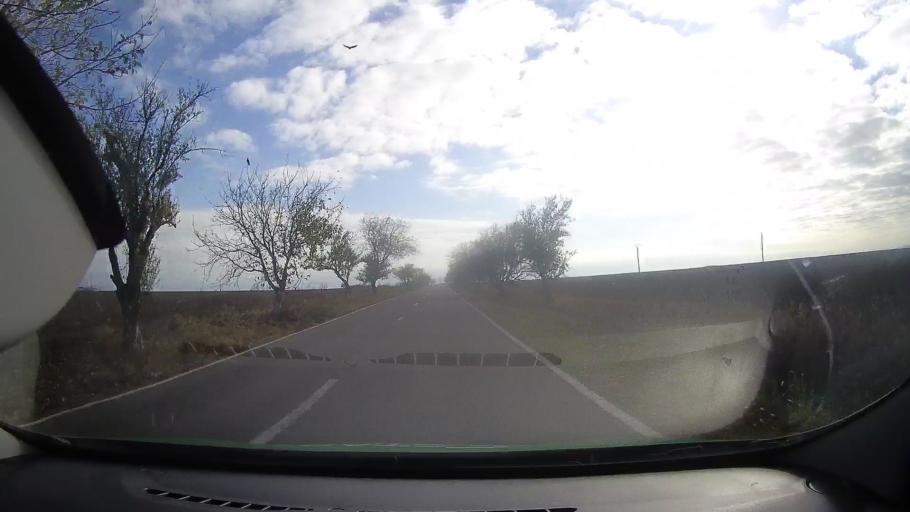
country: RO
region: Tulcea
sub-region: Comuna Bestepe
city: Bestepe
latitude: 45.0793
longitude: 29.0395
